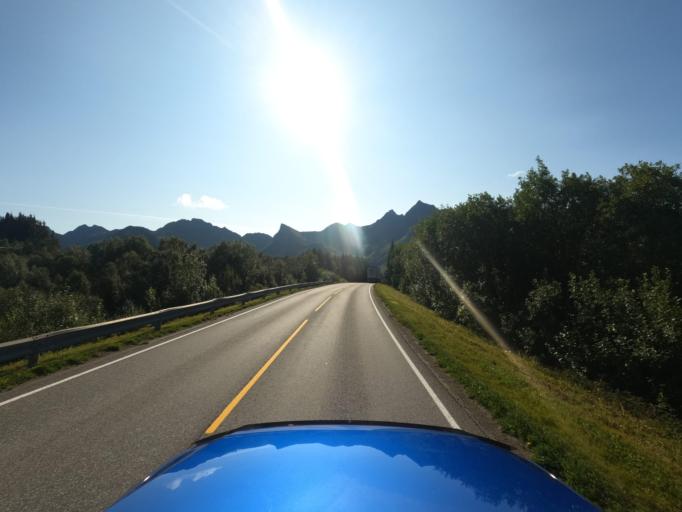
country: NO
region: Nordland
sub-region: Vagan
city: Kabelvag
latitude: 68.2496
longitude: 14.2777
